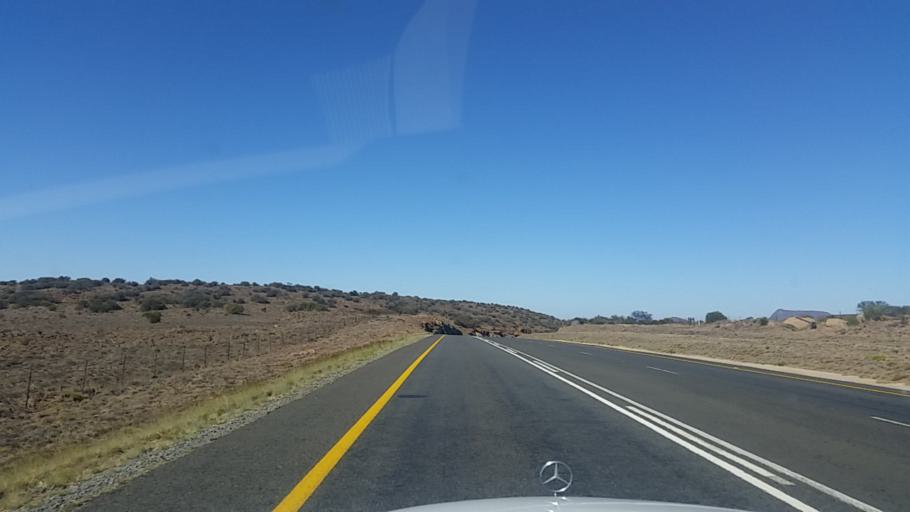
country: ZA
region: Eastern Cape
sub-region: Cacadu District Municipality
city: Graaff-Reinet
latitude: -32.0547
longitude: 24.6133
